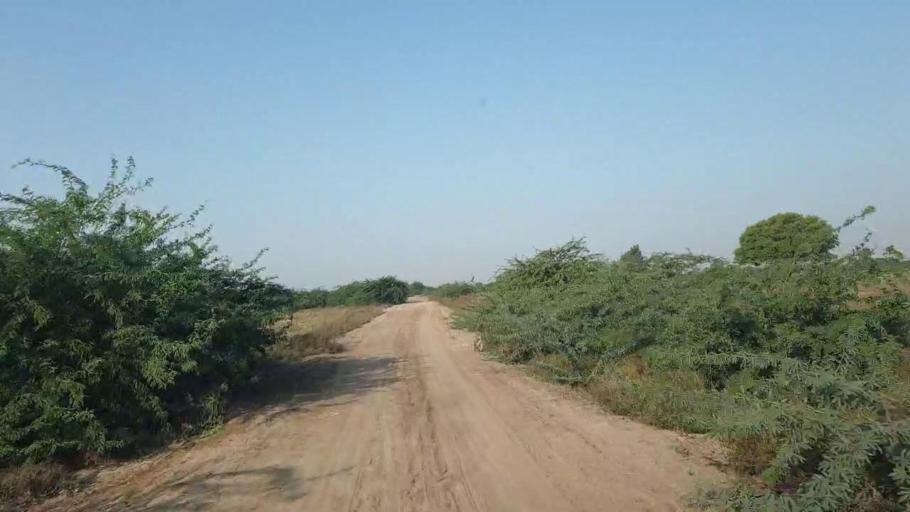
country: PK
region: Sindh
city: Badin
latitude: 24.4537
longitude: 68.7251
